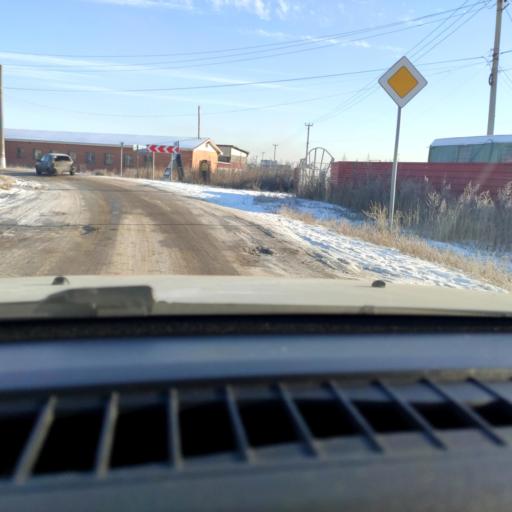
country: RU
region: Samara
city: Podstepki
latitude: 53.5203
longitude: 49.1447
